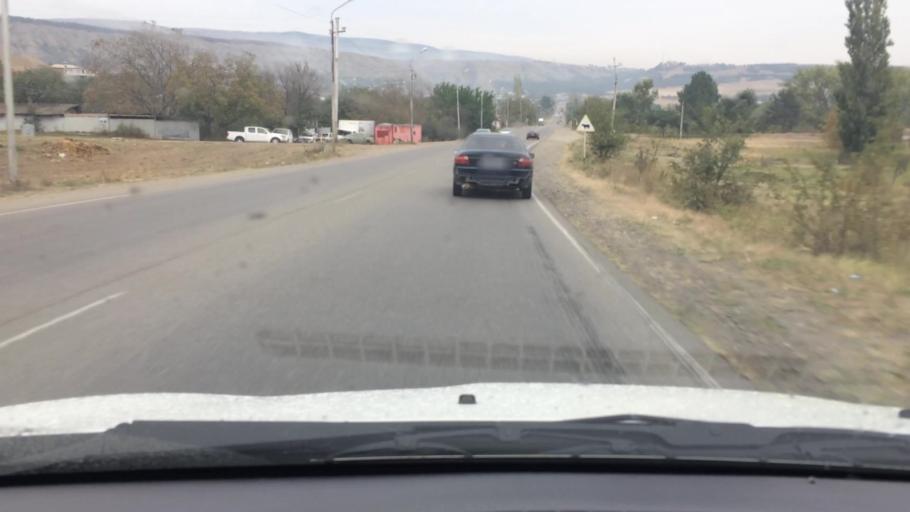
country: GE
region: T'bilisi
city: Tbilisi
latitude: 41.6028
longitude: 44.7794
